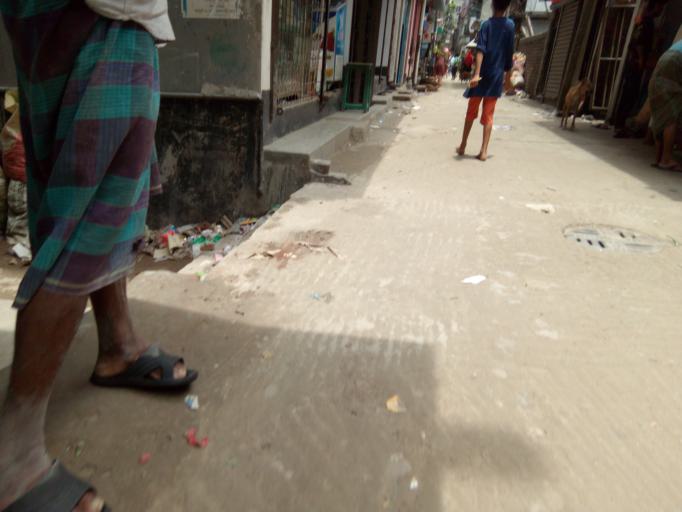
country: BD
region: Dhaka
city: Azimpur
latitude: 23.7179
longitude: 90.3667
